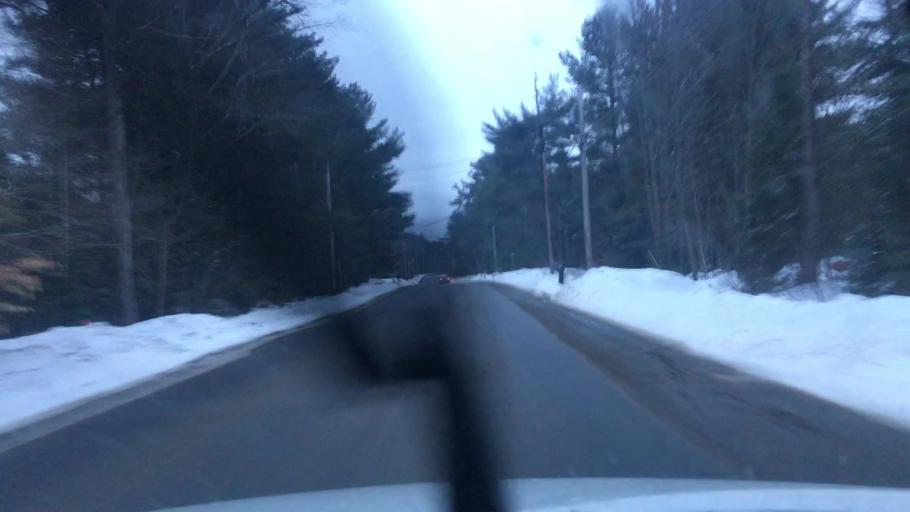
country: US
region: Maine
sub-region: Kennebec County
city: Oakland
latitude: 44.6240
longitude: -69.7272
